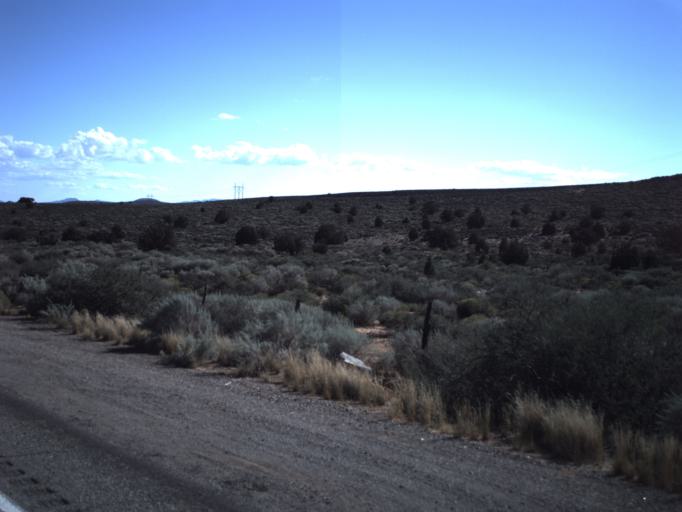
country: US
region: Utah
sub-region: Washington County
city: Toquerville
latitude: 37.2653
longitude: -113.2954
